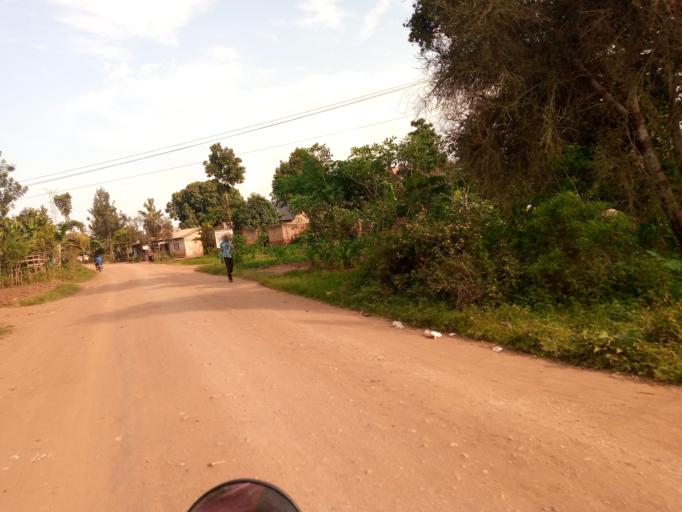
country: UG
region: Eastern Region
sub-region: Mbale District
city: Mbale
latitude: 1.0605
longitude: 34.1549
